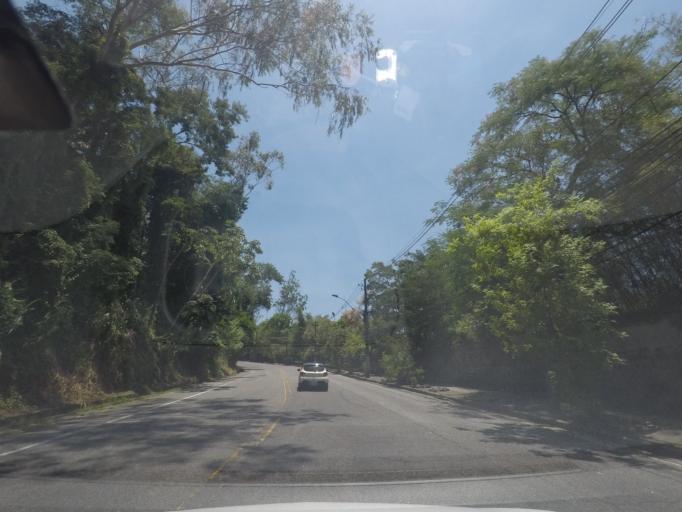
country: BR
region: Rio de Janeiro
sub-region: Niteroi
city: Niteroi
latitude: -22.9162
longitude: -43.0647
